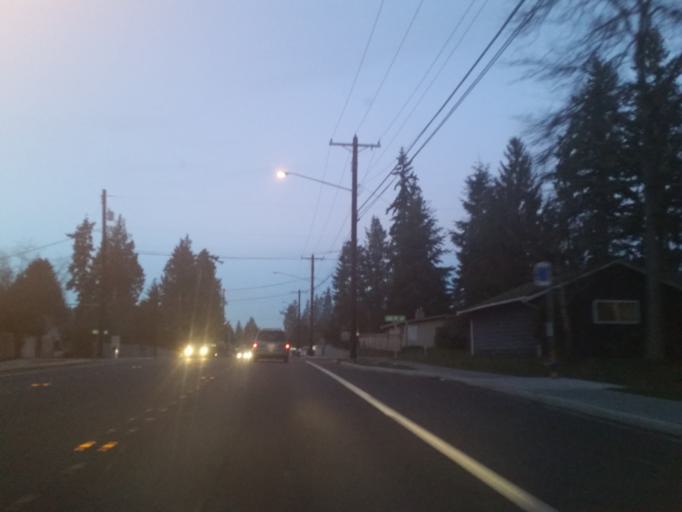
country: US
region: Washington
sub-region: Snohomish County
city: Meadowdale
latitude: 47.8505
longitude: -122.3036
